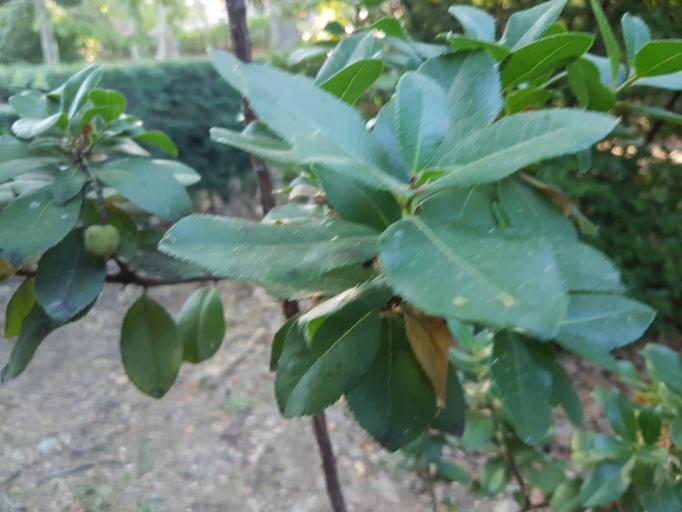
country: ES
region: Madrid
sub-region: Provincia de Madrid
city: Moncloa-Aravaca
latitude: 40.4496
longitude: -3.7212
